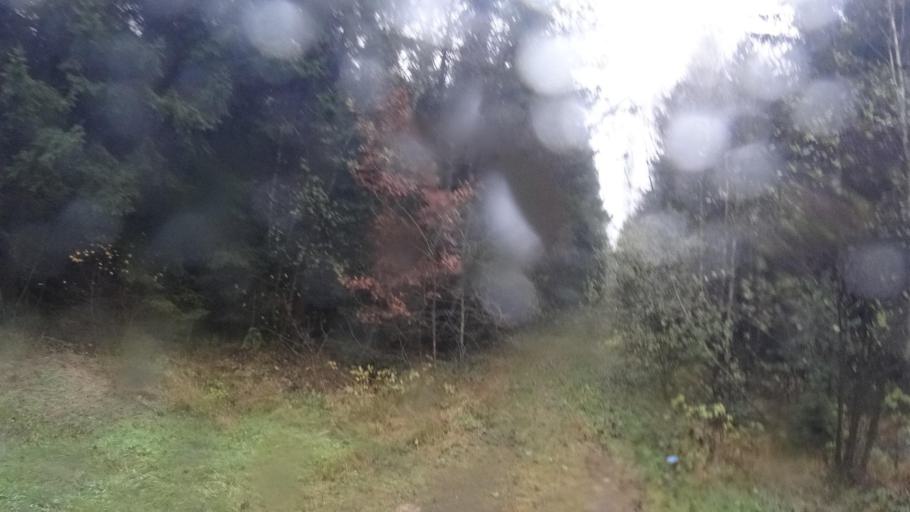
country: DE
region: Rheinland-Pfalz
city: Maisborn
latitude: 50.0932
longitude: 7.5887
